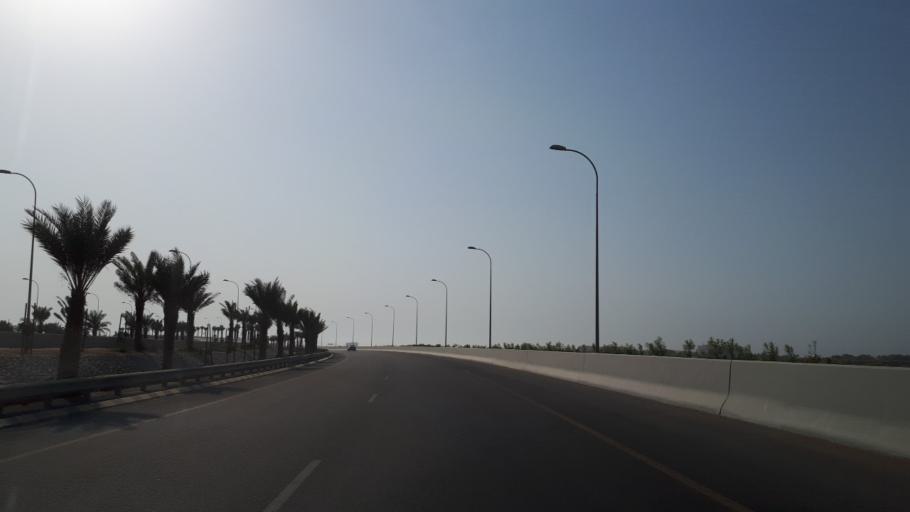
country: OM
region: Muhafazat Masqat
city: Bawshar
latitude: 23.5959
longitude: 58.3355
